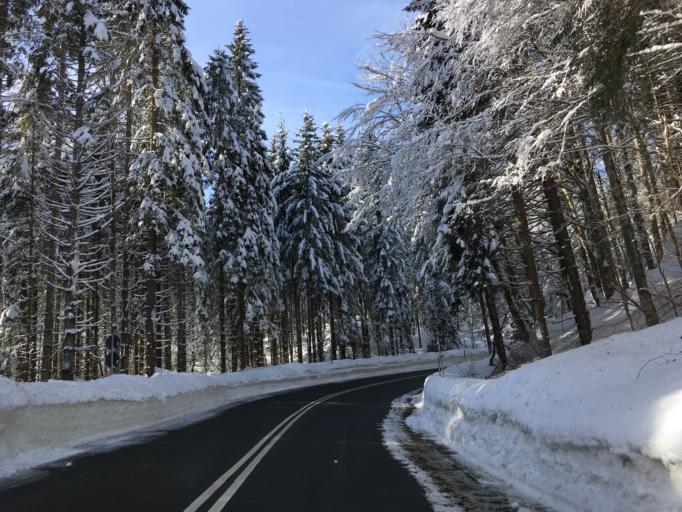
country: DE
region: Bavaria
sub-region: Upper Bavaria
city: Burg Unter-Falkenstein
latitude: 47.6710
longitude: 12.0785
